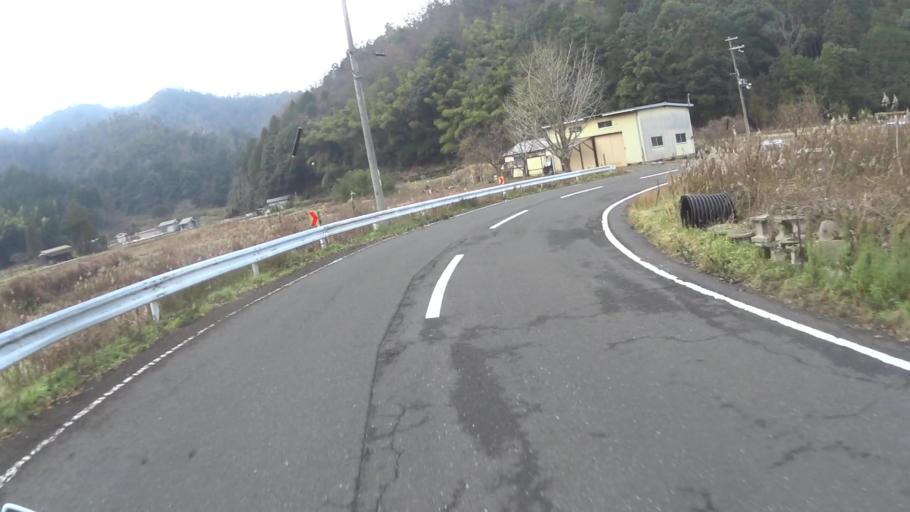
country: JP
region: Kyoto
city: Maizuru
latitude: 35.4451
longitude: 135.3902
